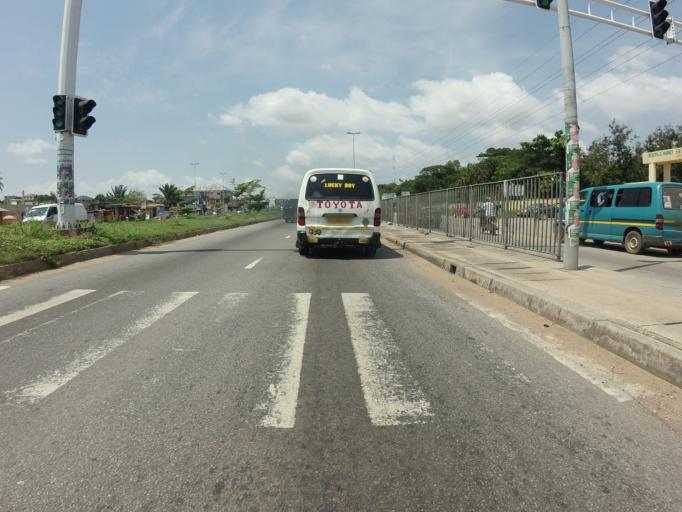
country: GH
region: Greater Accra
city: Gbawe
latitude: 5.5898
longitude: -0.2838
